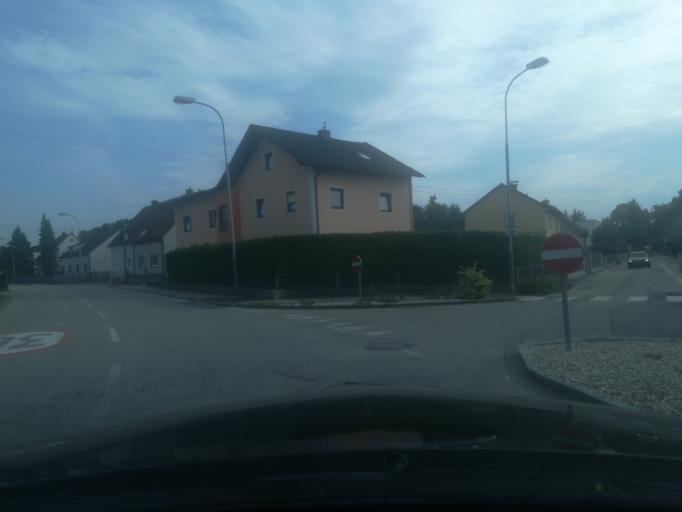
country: AT
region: Upper Austria
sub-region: Wels-Land
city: Marchtrenk
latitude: 48.1996
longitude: 14.1269
